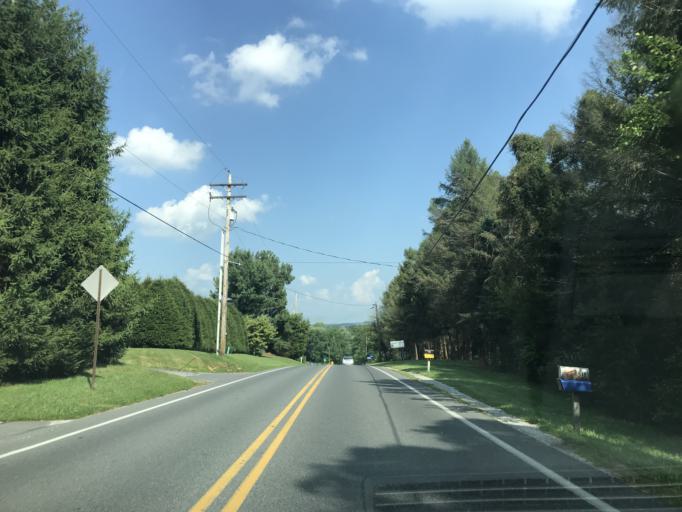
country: US
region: Pennsylvania
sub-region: York County
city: Parkville
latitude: 39.7924
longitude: -76.9291
